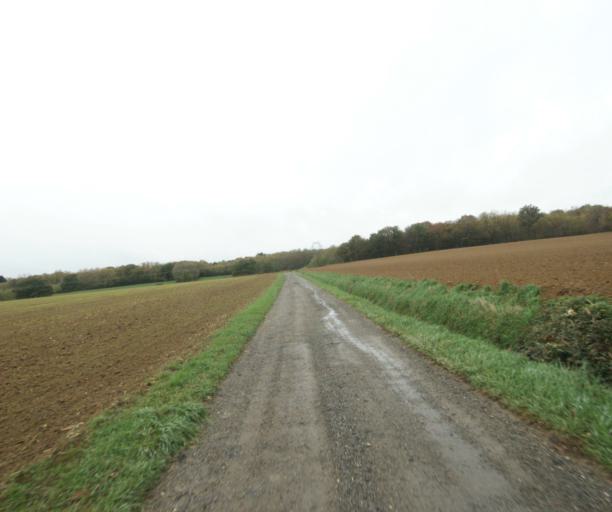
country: FR
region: Rhone-Alpes
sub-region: Departement de l'Ain
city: Pont-de-Vaux
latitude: 46.4823
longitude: 4.8558
